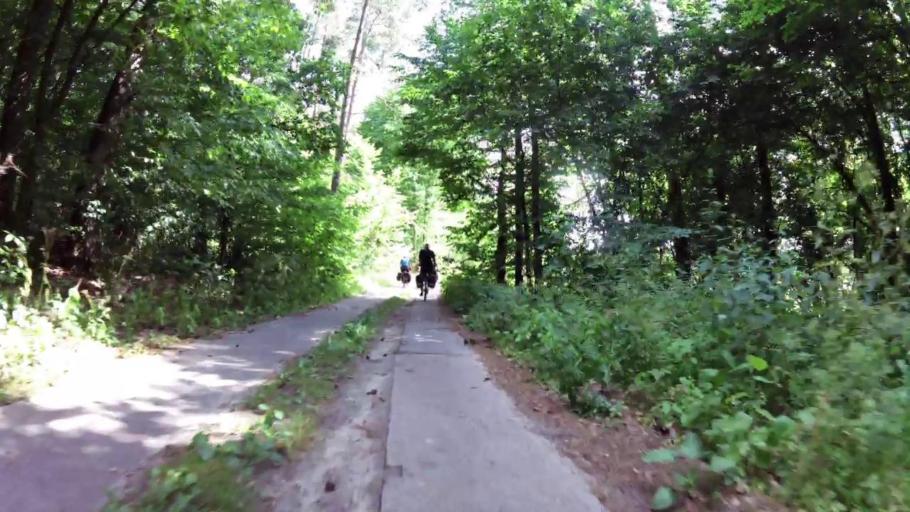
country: PL
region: West Pomeranian Voivodeship
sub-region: Powiat lobeski
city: Lobez
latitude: 53.6451
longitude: 15.5816
